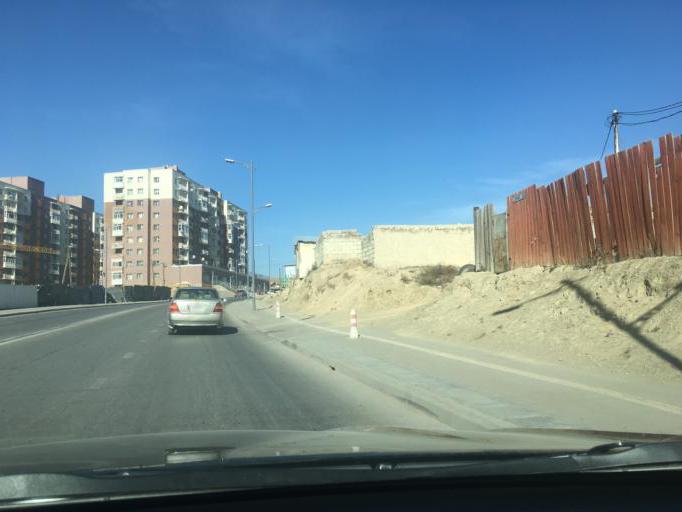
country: MN
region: Ulaanbaatar
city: Ulaanbaatar
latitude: 47.9144
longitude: 106.7812
